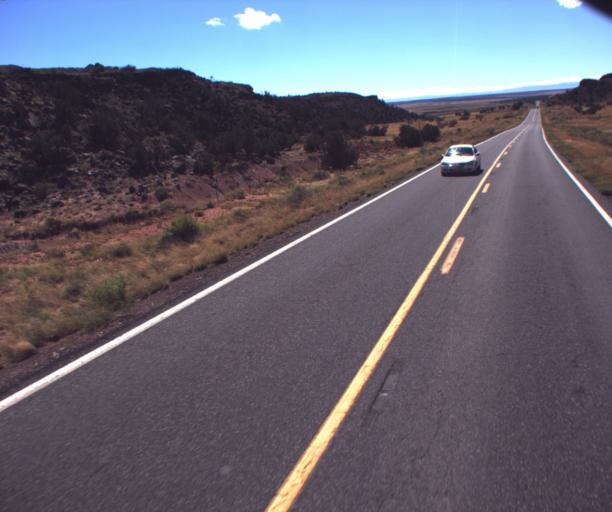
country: US
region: Arizona
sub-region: Apache County
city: Saint Johns
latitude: 34.7549
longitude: -109.2439
